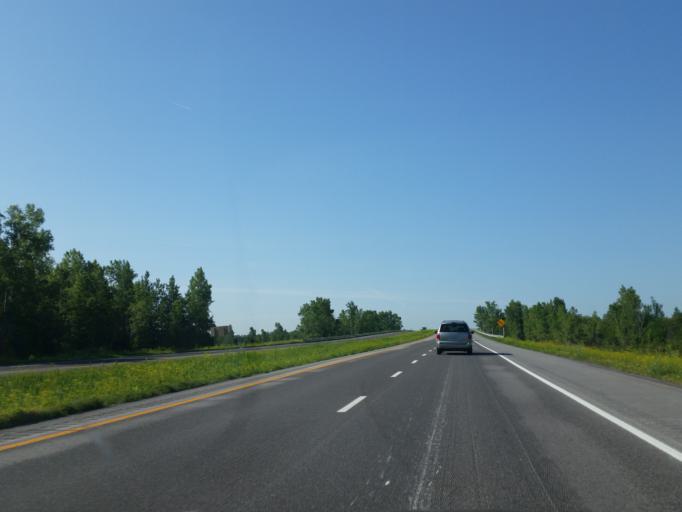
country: CA
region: Quebec
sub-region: Monteregie
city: Napierville
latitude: 45.2428
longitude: -73.4733
